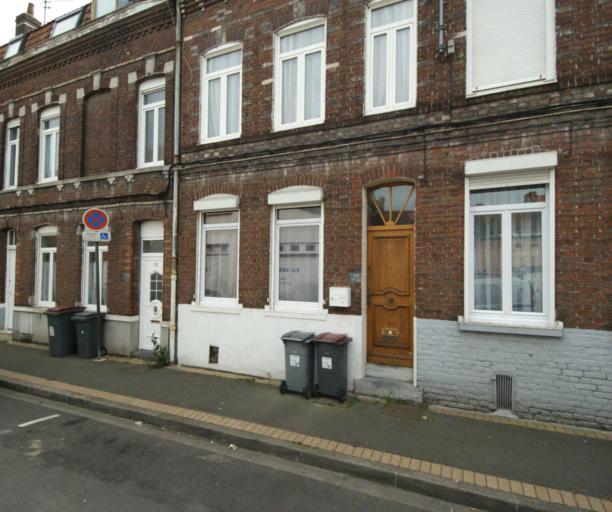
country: FR
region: Nord-Pas-de-Calais
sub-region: Departement du Nord
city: Haubourdin
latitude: 50.6108
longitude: 2.9921
